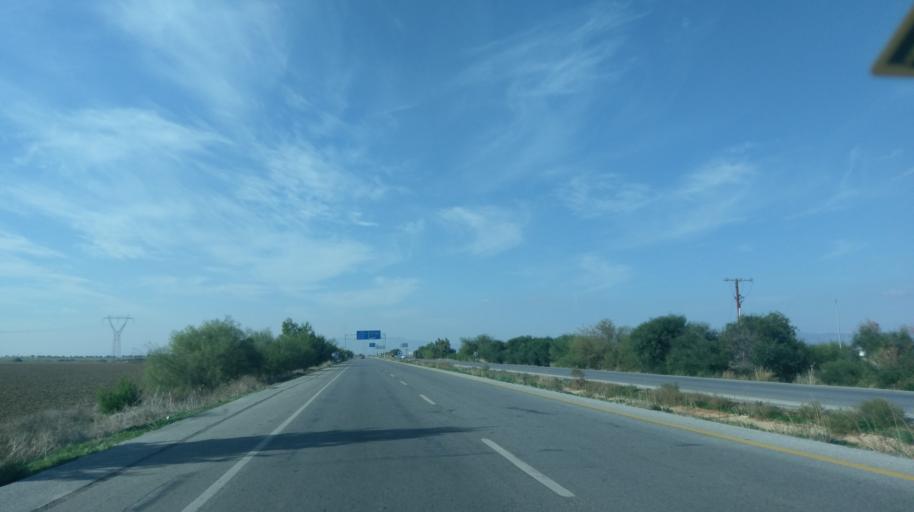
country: CY
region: Ammochostos
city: Acheritou
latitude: 35.1652
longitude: 33.8261
